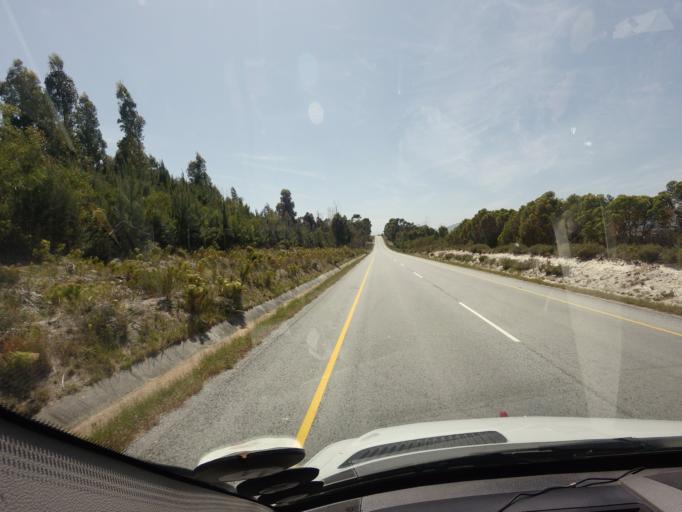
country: ZA
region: Western Cape
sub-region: Overberg District Municipality
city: Hermanus
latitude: -34.3205
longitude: 19.1126
